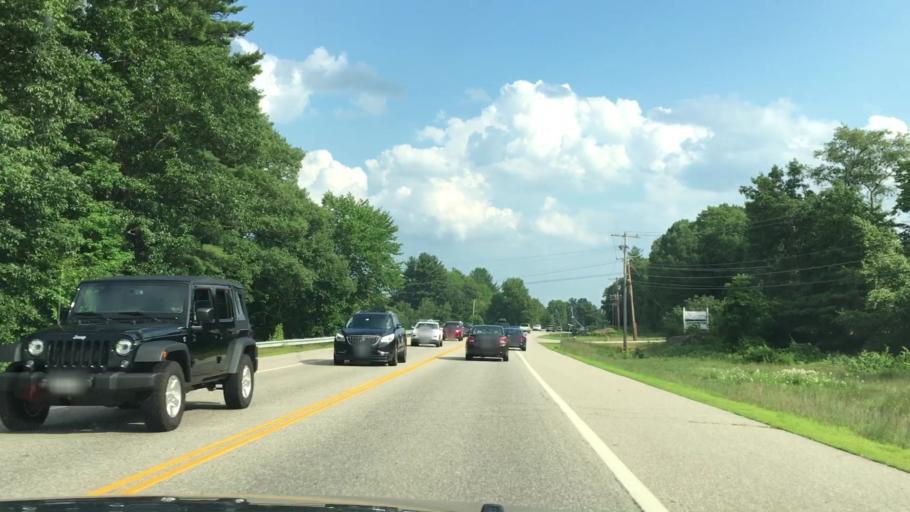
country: US
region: New Hampshire
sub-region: Strafford County
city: Farmington
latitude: 43.3551
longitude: -71.0288
